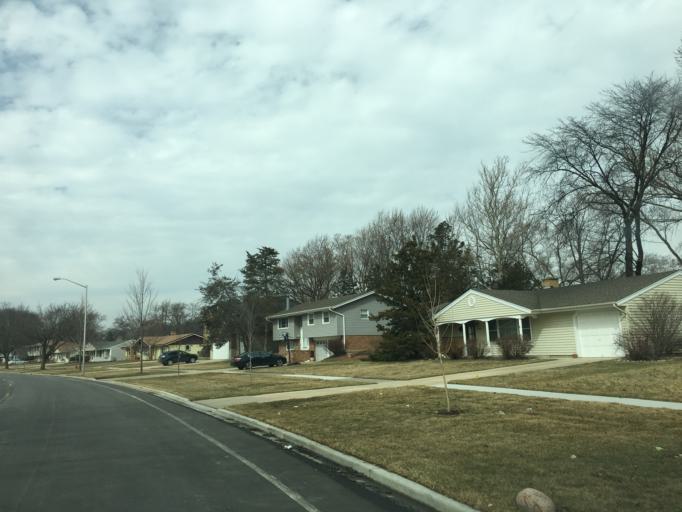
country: US
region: Illinois
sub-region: Cook County
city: Schaumburg
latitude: 42.0191
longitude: -88.1105
